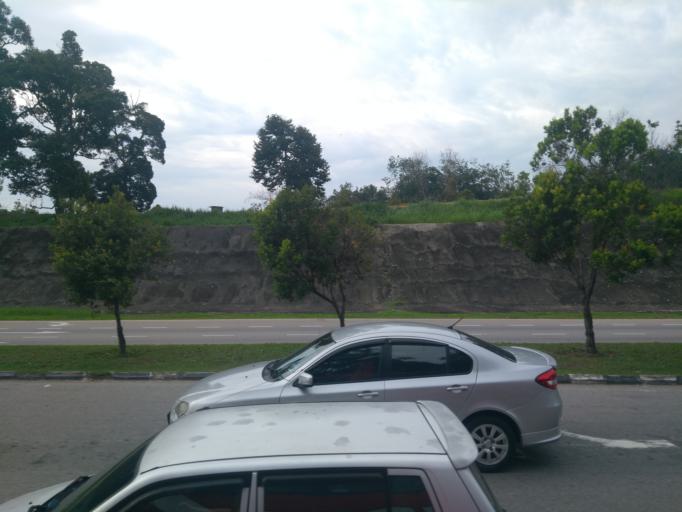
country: MY
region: Melaka
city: Kampung Ayer Keroh
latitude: 2.2868
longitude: 102.2635
